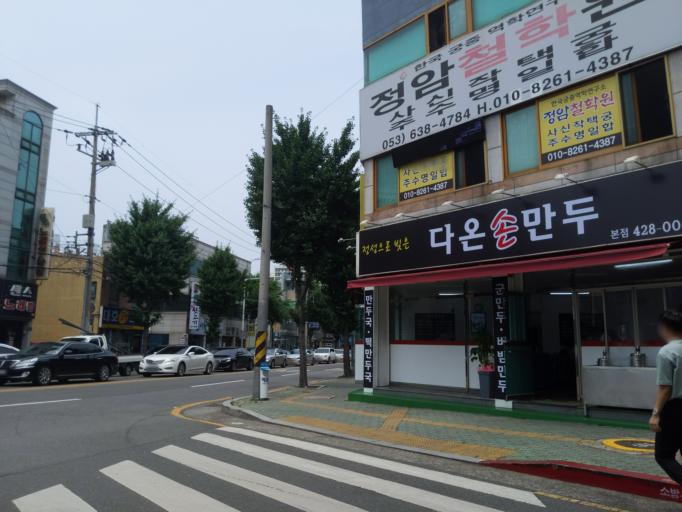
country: KR
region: Daegu
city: Hwawon
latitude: 35.8091
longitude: 128.5270
